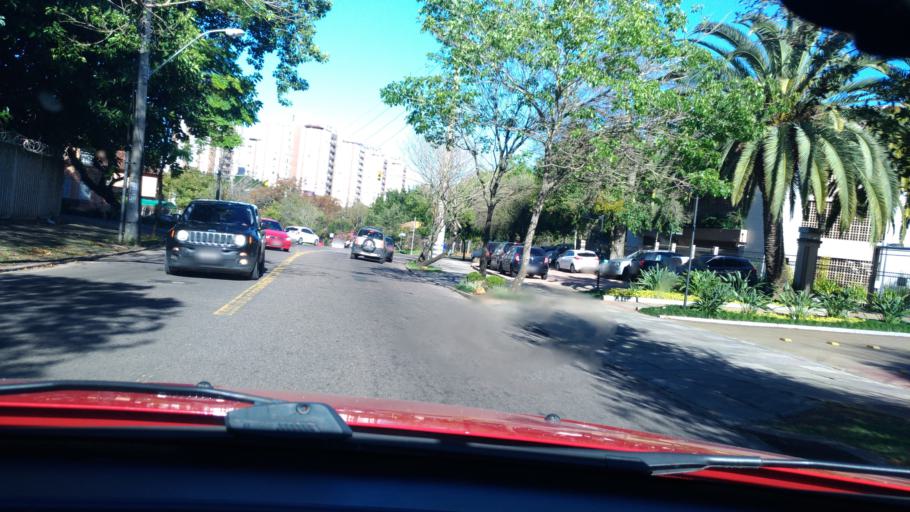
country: BR
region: Rio Grande do Sul
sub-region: Porto Alegre
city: Porto Alegre
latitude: -30.0182
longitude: -51.1787
